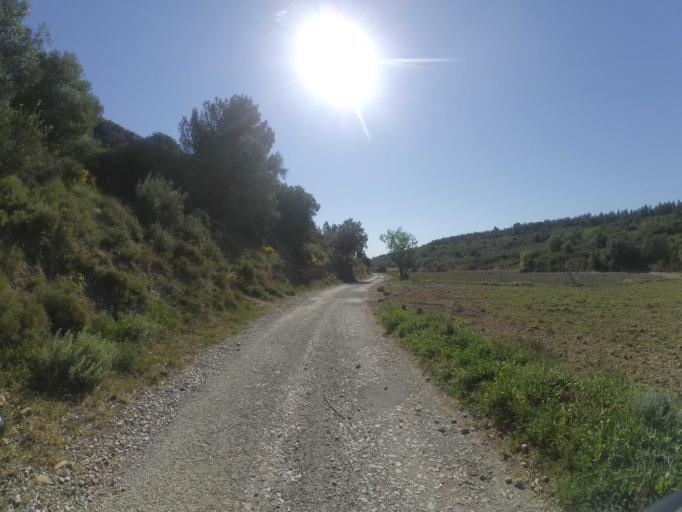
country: FR
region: Languedoc-Roussillon
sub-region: Departement des Pyrenees-Orientales
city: Baixas
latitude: 42.7584
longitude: 2.7909
